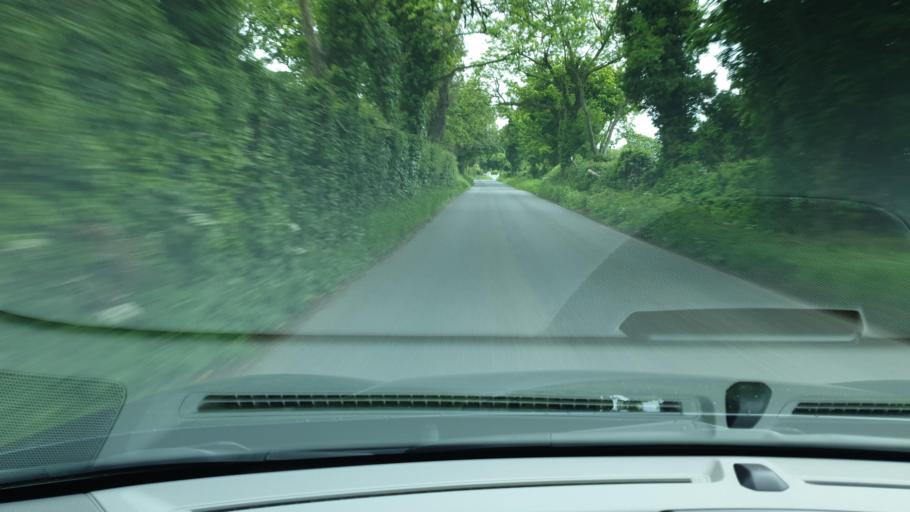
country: IE
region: Leinster
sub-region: An Mhi
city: Stamullin
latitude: 53.5570
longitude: -6.3162
